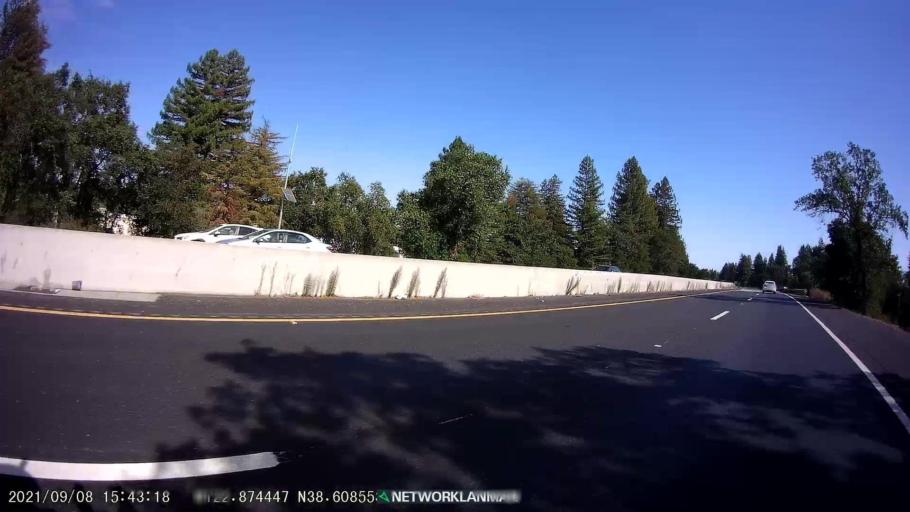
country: US
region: California
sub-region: Sonoma County
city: Healdsburg
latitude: 38.6082
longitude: -122.8742
